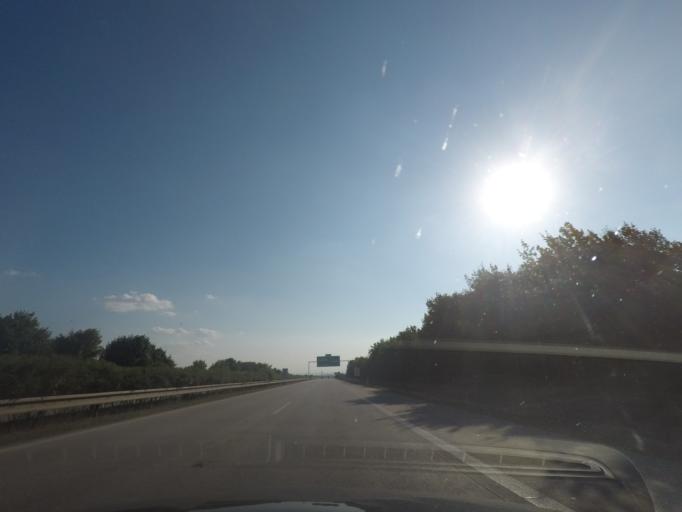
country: CZ
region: Olomoucky
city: Velky Tynec
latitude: 49.5665
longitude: 17.3344
